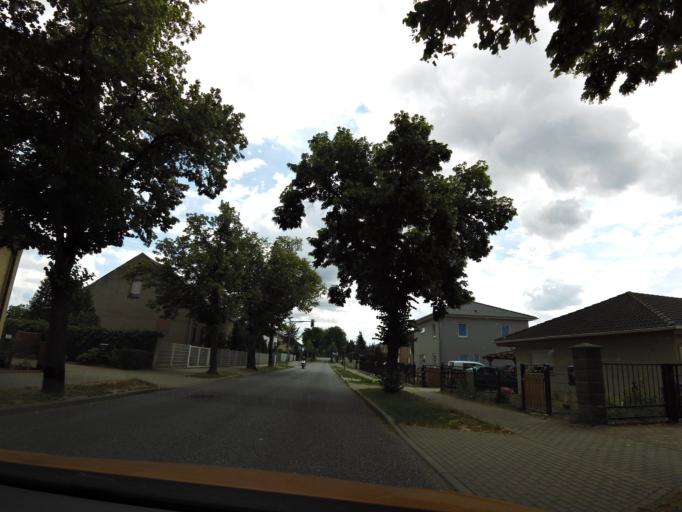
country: DE
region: Brandenburg
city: Grossbeeren
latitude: 52.3414
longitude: 13.3645
